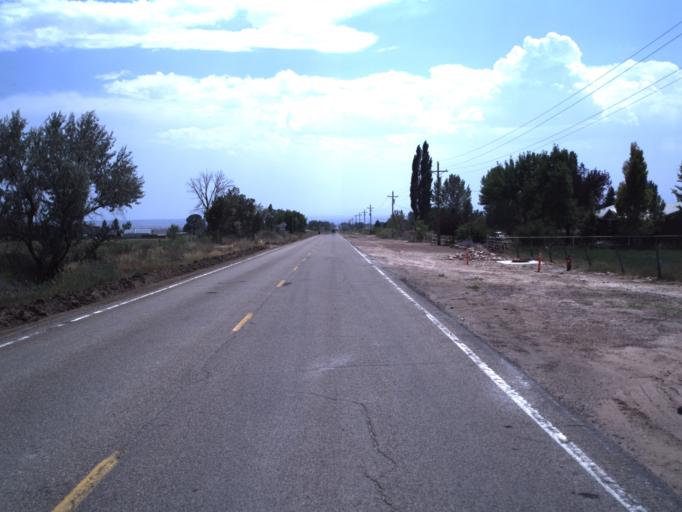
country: US
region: Utah
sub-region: Duchesne County
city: Roosevelt
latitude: 40.4245
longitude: -110.0300
